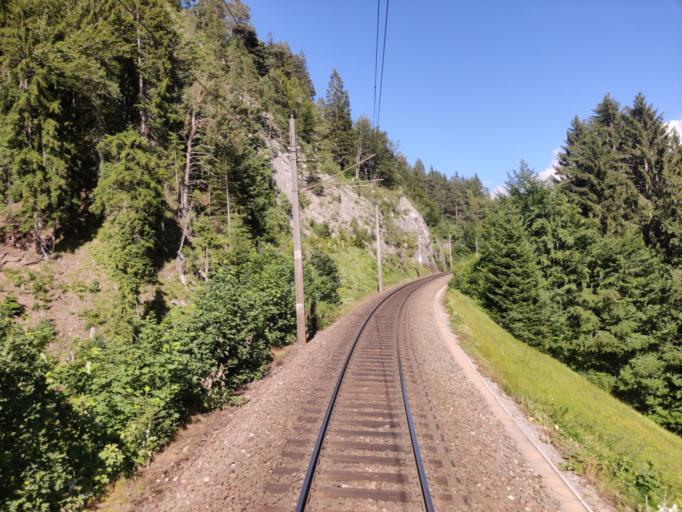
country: AT
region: Vorarlberg
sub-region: Politischer Bezirk Bludenz
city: Dalaas
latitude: 47.1331
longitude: 10.0360
